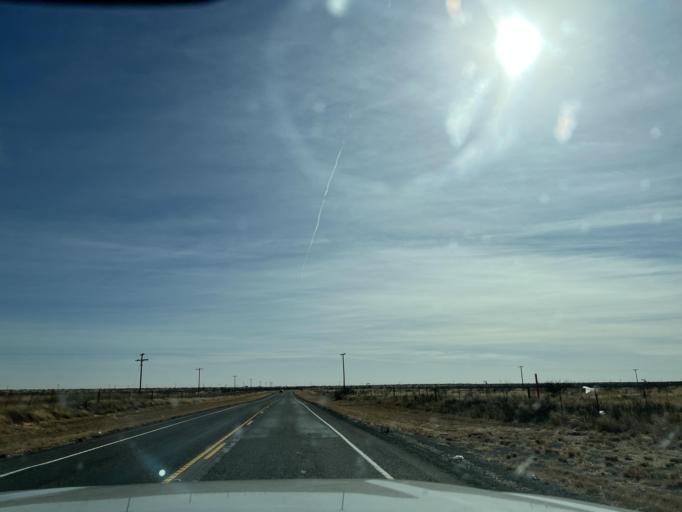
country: US
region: Texas
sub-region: Andrews County
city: Andrews
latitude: 32.4419
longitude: -102.4429
